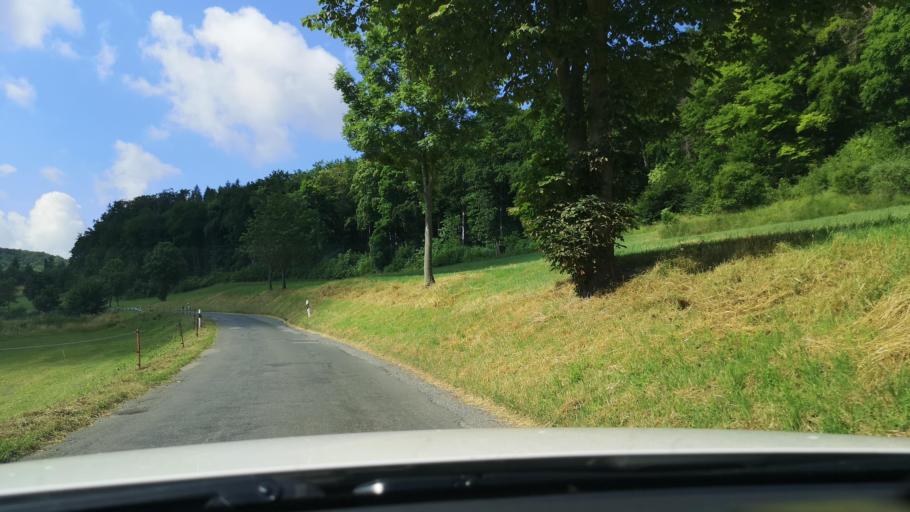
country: DE
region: Thuringia
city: Tautenburg
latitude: 50.9972
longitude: 11.7155
